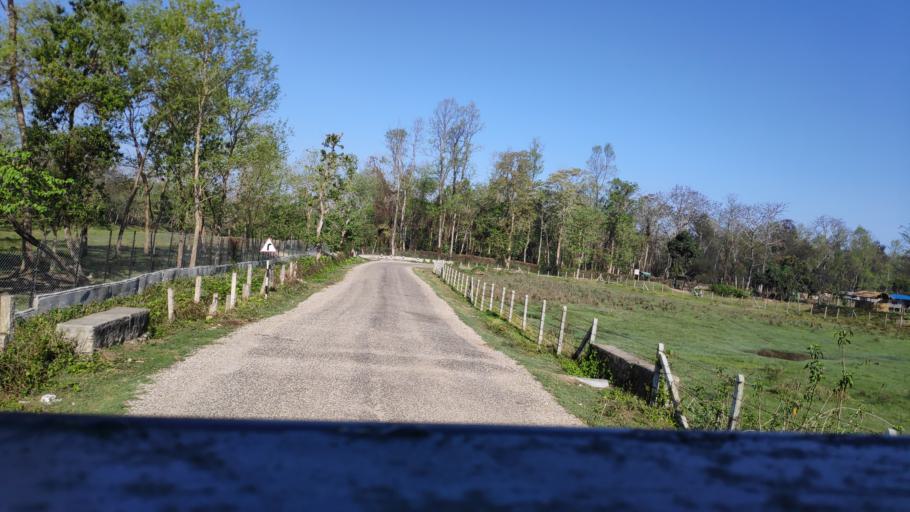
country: NP
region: Central Region
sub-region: Narayani Zone
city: Bharatpur
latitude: 27.5695
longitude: 84.5182
